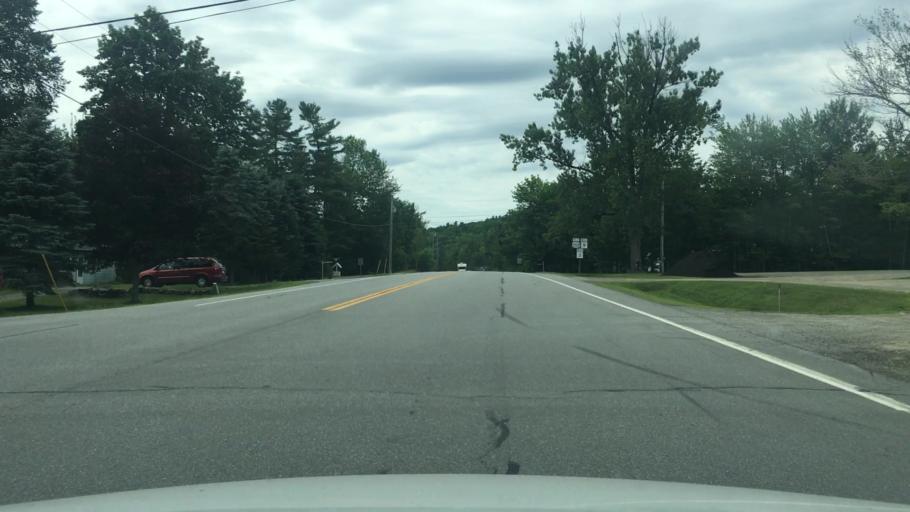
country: US
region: Maine
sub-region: Kennebec County
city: Windsor
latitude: 44.3754
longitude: -69.6256
